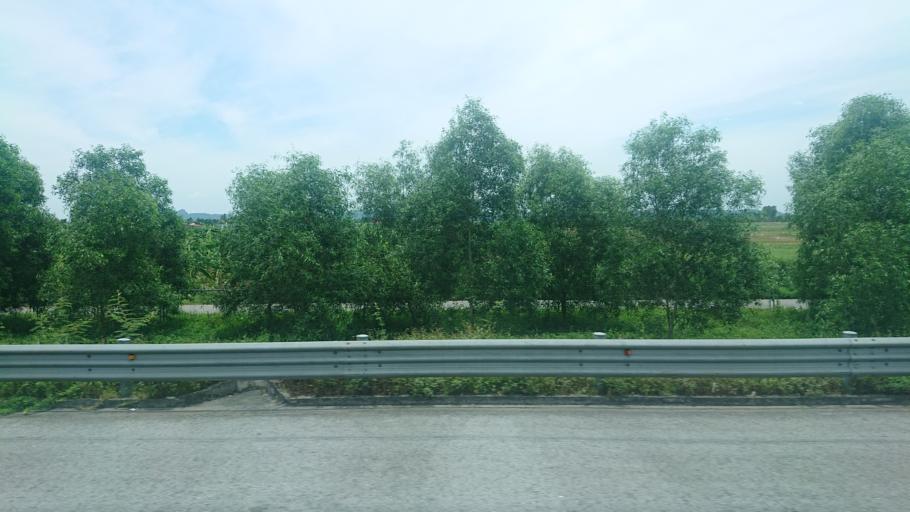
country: VN
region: Hai Phong
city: An Lao
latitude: 20.7857
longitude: 106.5611
